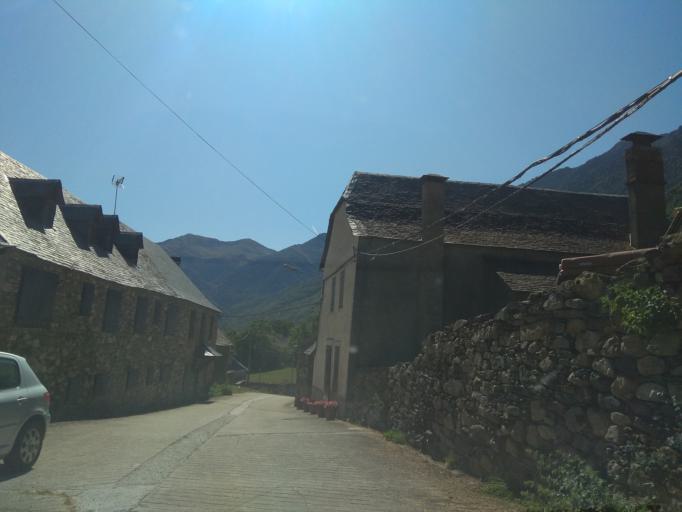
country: ES
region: Catalonia
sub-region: Provincia de Lleida
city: Les
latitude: 42.7527
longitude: 0.6963
